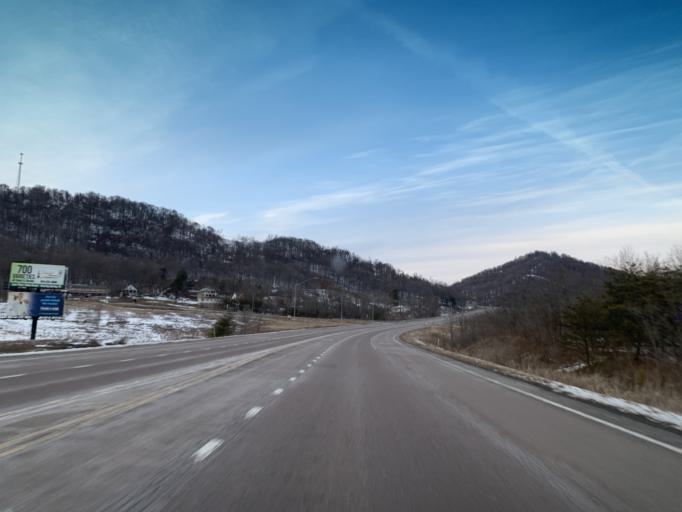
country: US
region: Maryland
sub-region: Allegany County
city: Cumberland
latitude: 39.7129
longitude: -78.7025
